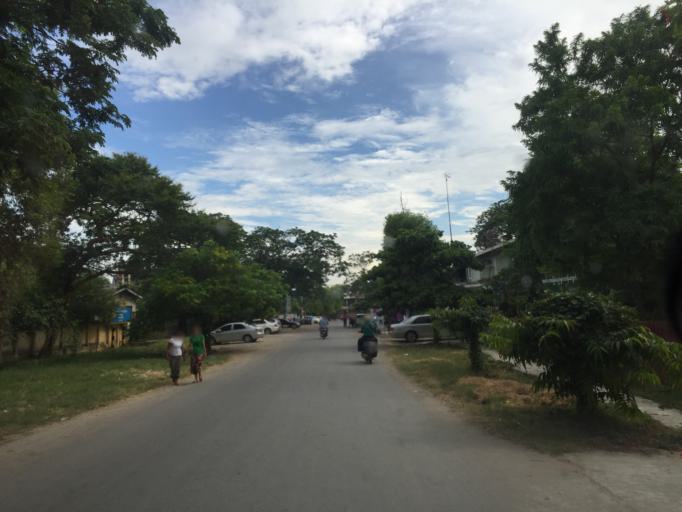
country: MM
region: Mandalay
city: Mandalay
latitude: 21.9744
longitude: 96.1048
